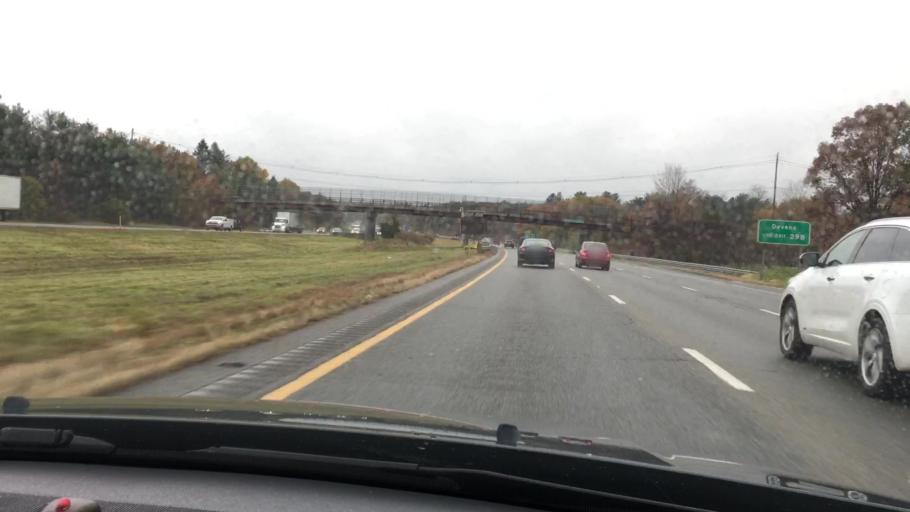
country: US
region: Massachusetts
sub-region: Middlesex County
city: Littleton Common
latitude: 42.5466
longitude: -71.4852
